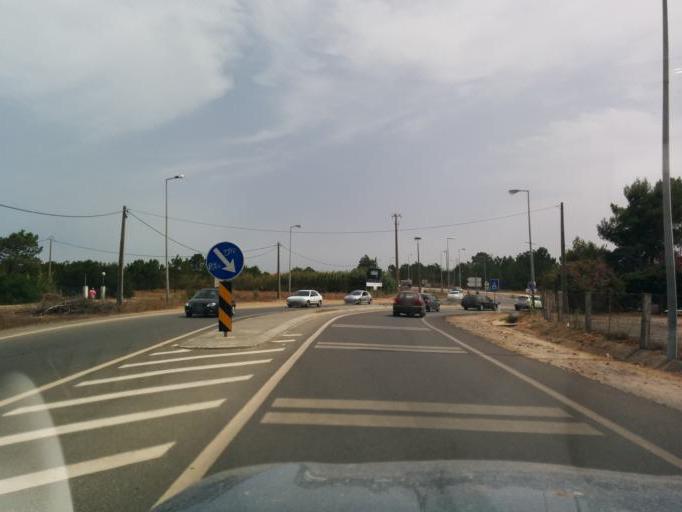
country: PT
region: Beja
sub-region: Odemira
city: Vila Nova de Milfontes
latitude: 37.7329
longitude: -8.7727
